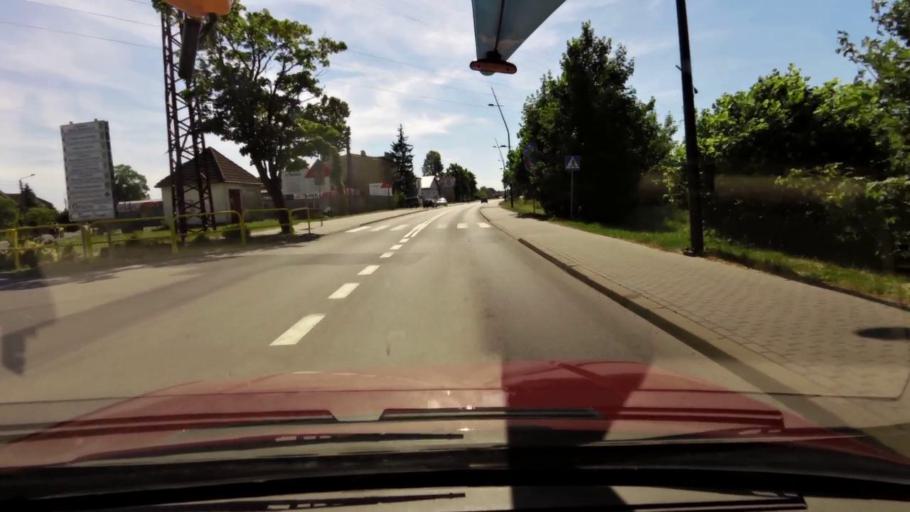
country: PL
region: Pomeranian Voivodeship
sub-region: Powiat slupski
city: Kobylnica
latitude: 54.4464
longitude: 17.0072
